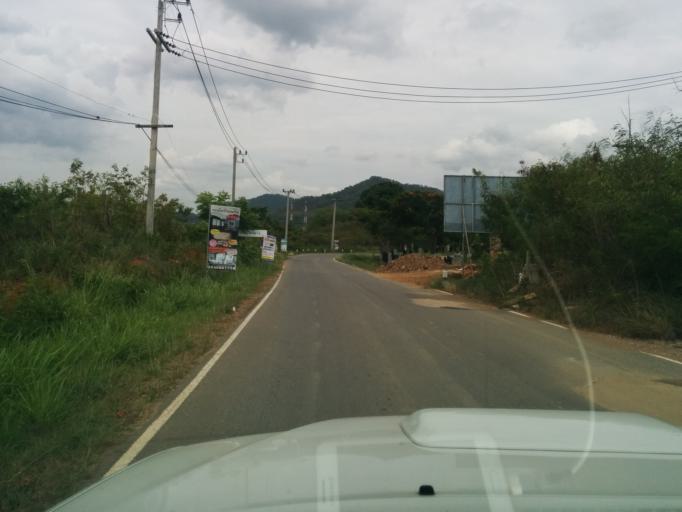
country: TH
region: Sara Buri
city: Muak Lek
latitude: 14.5619
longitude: 101.2522
